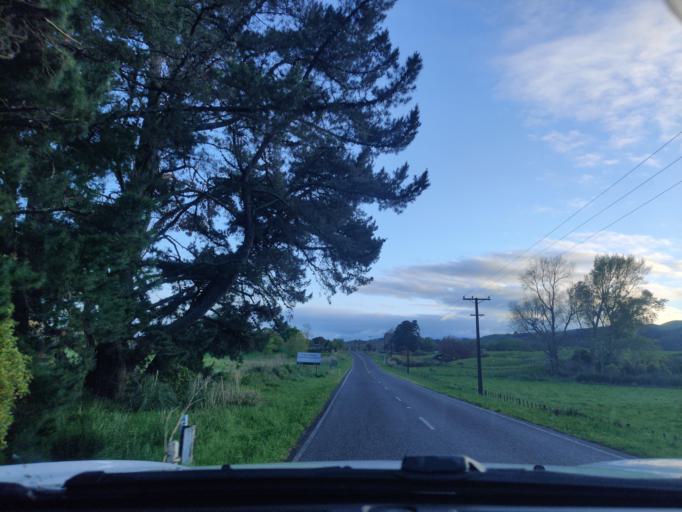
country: NZ
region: Manawatu-Wanganui
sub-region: Palmerston North City
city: Palmerston North
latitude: -40.3125
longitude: 175.7601
